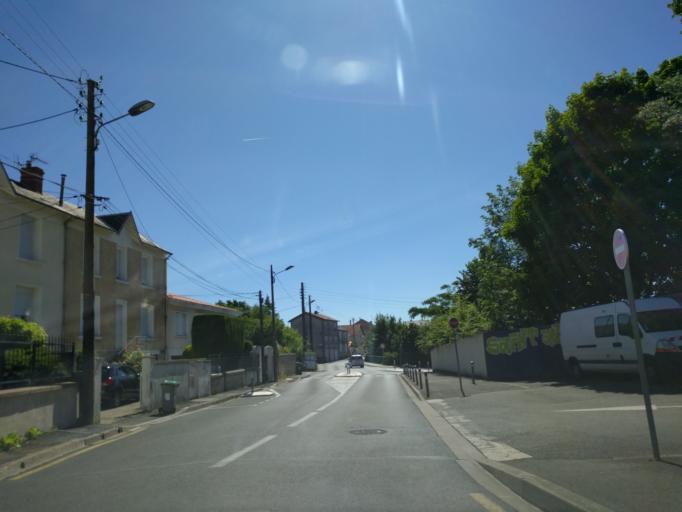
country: FR
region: Poitou-Charentes
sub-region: Departement des Deux-Sevres
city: Niort
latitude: 46.3276
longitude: -0.4452
